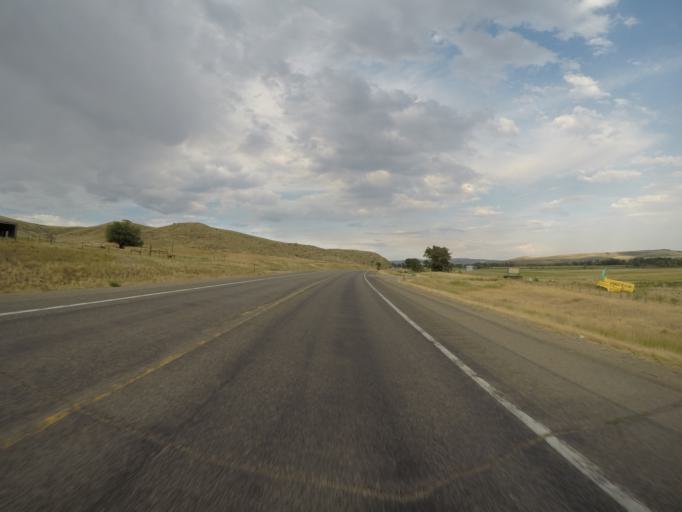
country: US
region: Colorado
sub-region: Moffat County
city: Craig
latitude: 40.5181
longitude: -107.4844
